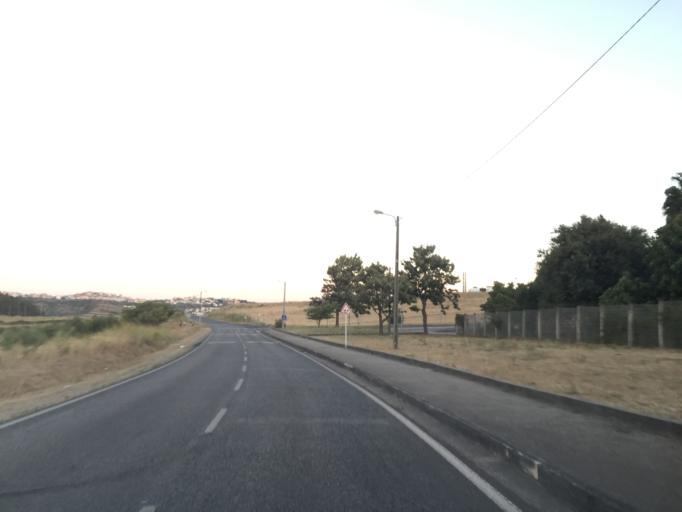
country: PT
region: Lisbon
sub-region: Odivelas
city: Povoa de Santo Adriao
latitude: 38.8114
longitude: -9.1744
